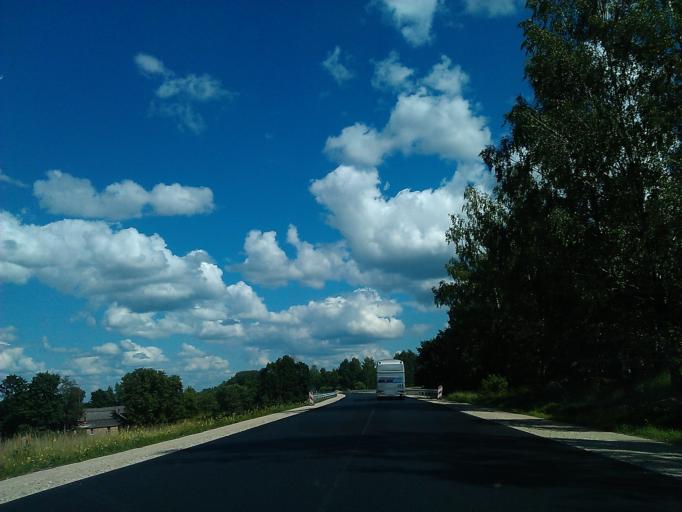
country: LV
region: Rezekne
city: Rezekne
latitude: 56.5330
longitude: 27.1752
